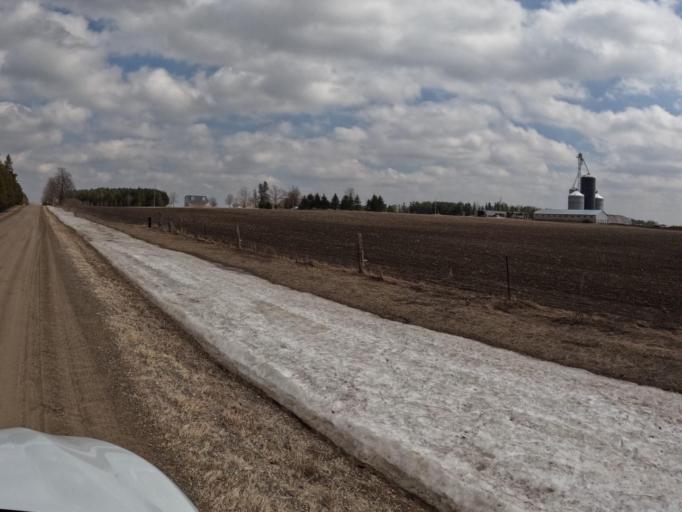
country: CA
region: Ontario
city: Shelburne
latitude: 44.0295
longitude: -80.2455
